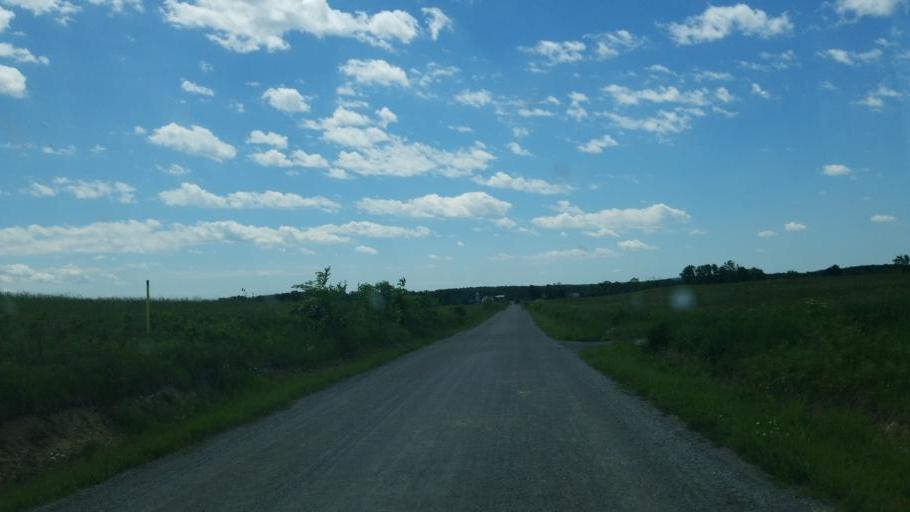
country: US
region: Ohio
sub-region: Geauga County
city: Middlefield
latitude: 41.3971
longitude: -80.9900
